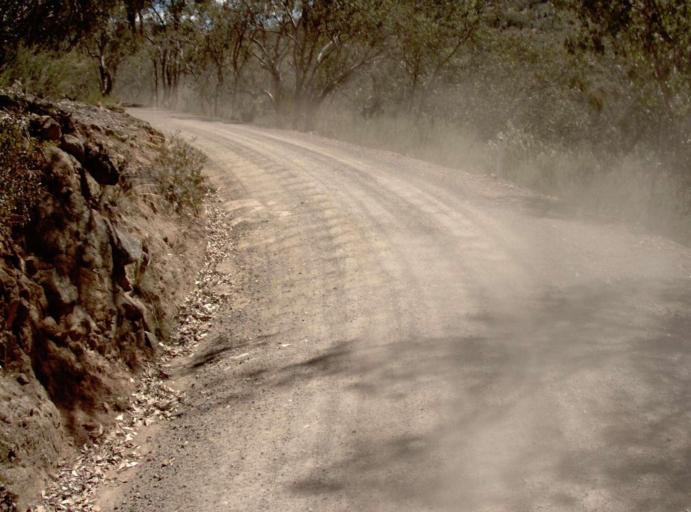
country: AU
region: New South Wales
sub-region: Snowy River
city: Jindabyne
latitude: -37.0710
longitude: 148.4976
